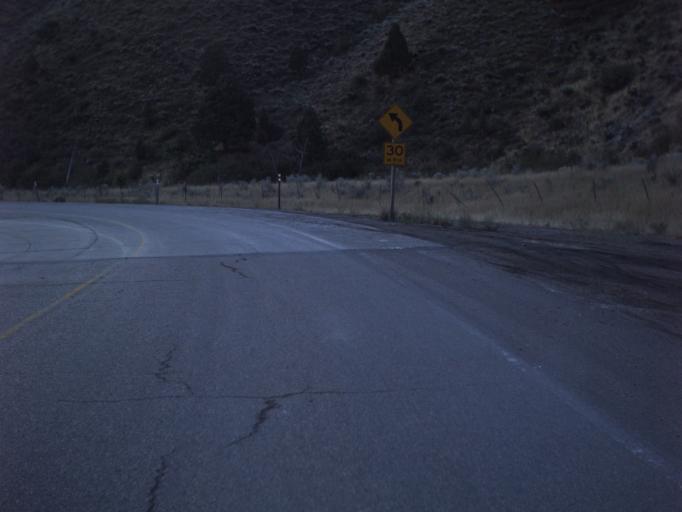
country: US
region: Utah
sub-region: Morgan County
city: Morgan
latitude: 41.0575
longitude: -111.5397
